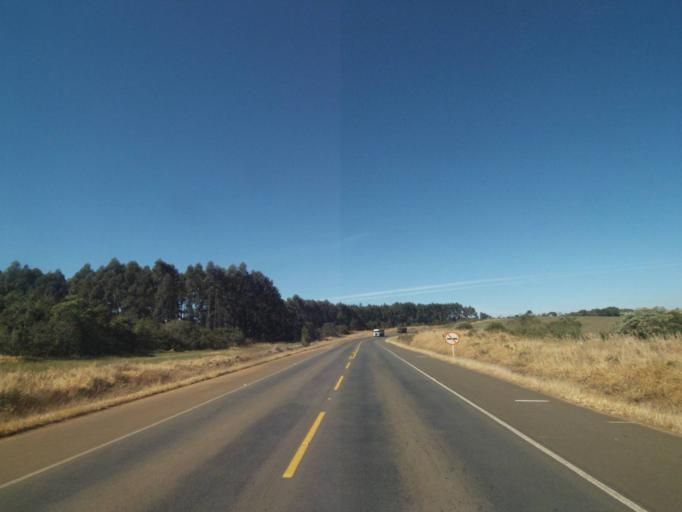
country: BR
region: Parana
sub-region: Tibagi
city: Tibagi
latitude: -24.6861
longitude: -50.4411
